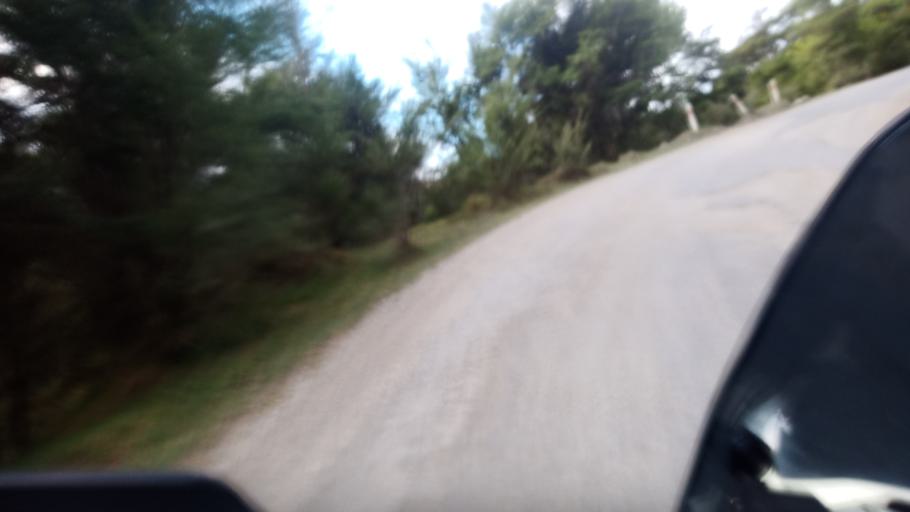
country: NZ
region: Gisborne
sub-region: Gisborne District
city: Gisborne
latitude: -38.4778
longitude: 177.9730
